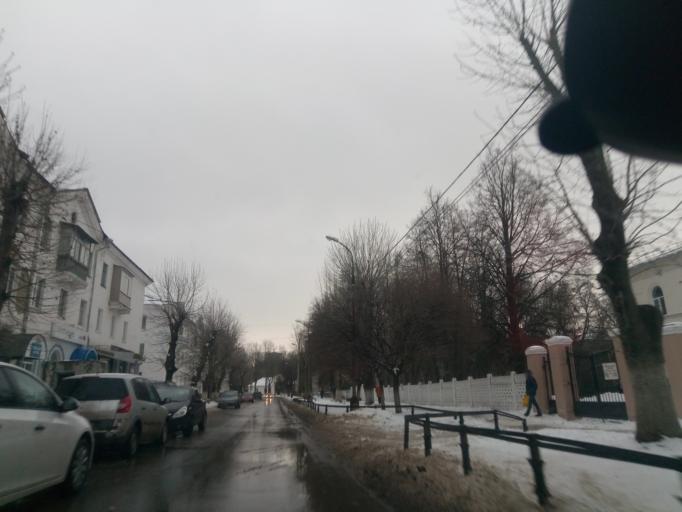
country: RU
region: Tula
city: Novomoskovsk
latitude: 54.0128
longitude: 38.2834
